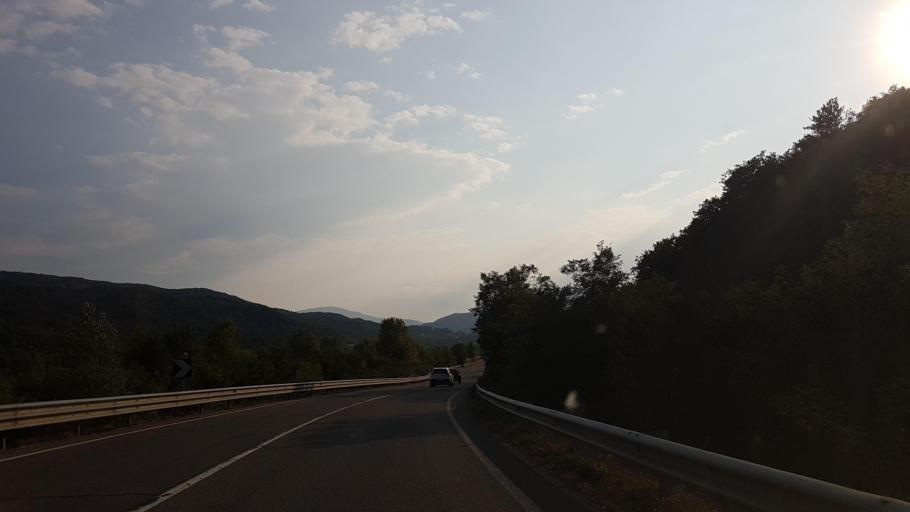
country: IT
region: Emilia-Romagna
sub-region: Provincia di Parma
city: Solignano
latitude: 44.6062
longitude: 9.9752
